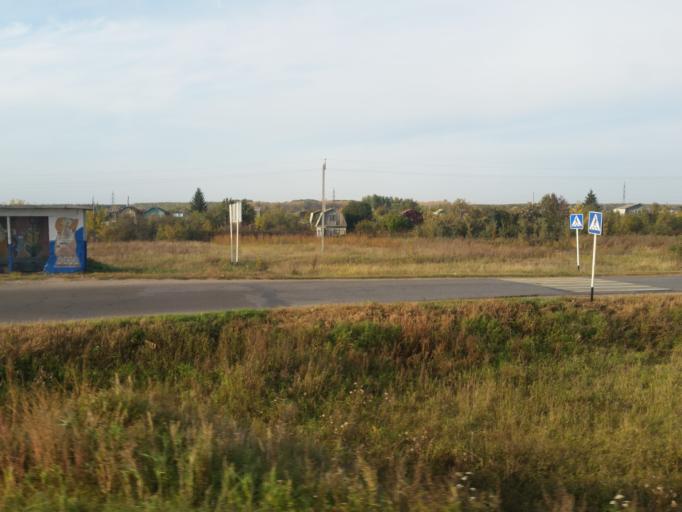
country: RU
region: Ulyanovsk
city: Cherdakly
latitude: 54.3545
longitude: 48.8896
